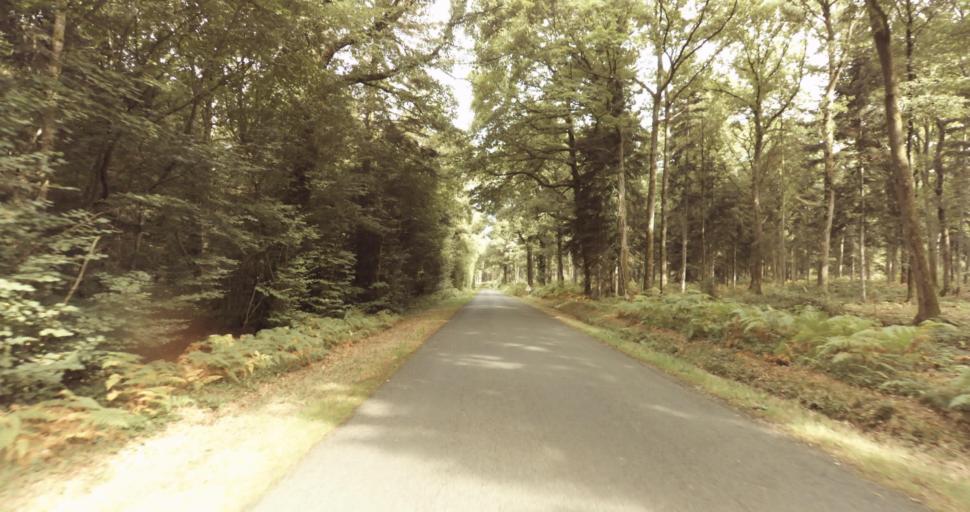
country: FR
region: Lower Normandy
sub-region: Departement de l'Orne
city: Vimoutiers
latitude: 48.9328
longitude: 0.2810
